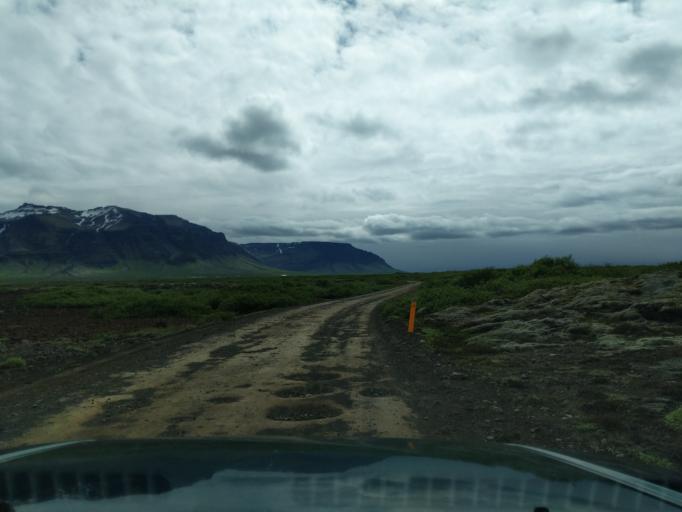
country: IS
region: West
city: Borgarnes
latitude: 64.8334
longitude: -22.3062
